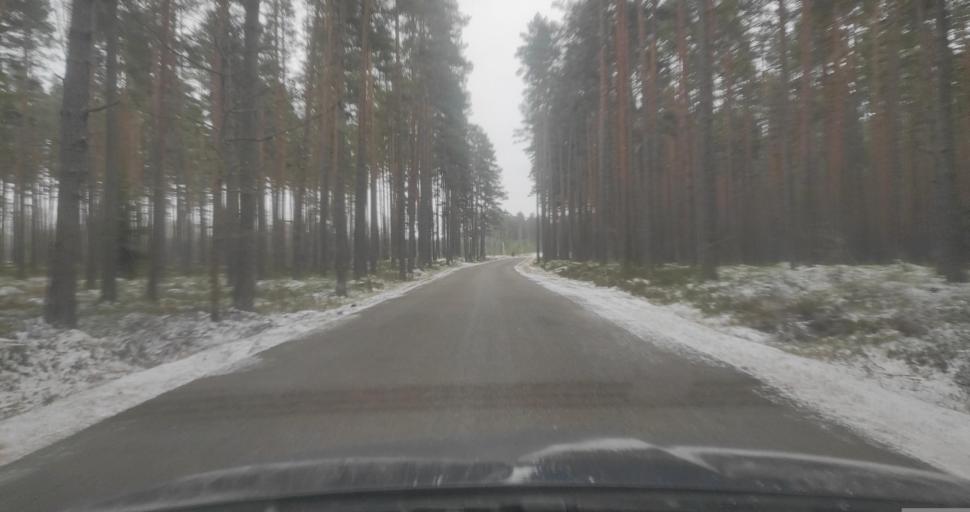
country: LV
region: Jurmala
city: Jurmala
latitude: 56.9138
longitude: 23.8218
